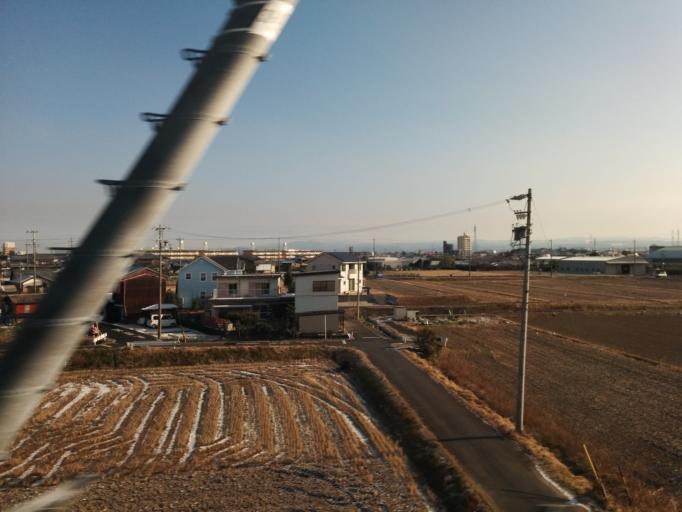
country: JP
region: Aichi
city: Anjo
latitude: 34.9432
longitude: 137.0842
